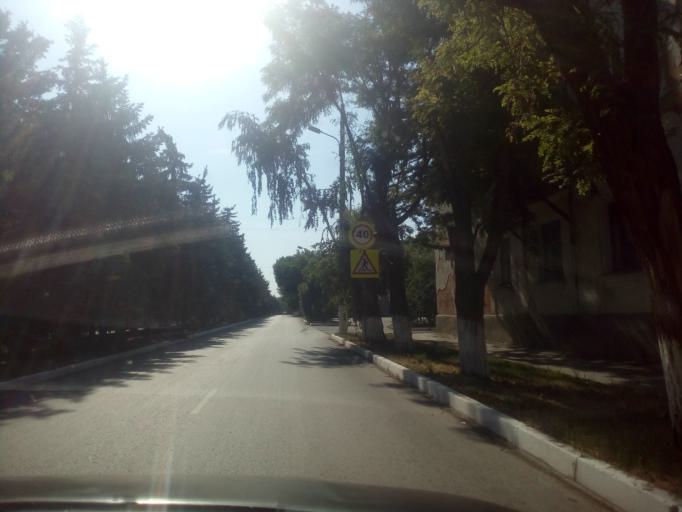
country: RU
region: Rostov
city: Sholokhovskiy
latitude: 48.2822
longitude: 41.0496
